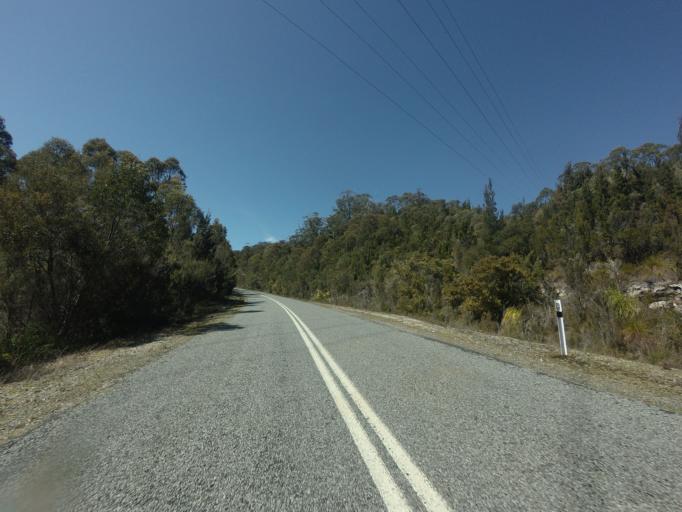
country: AU
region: Tasmania
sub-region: Huon Valley
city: Geeveston
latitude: -42.8126
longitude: 146.3893
